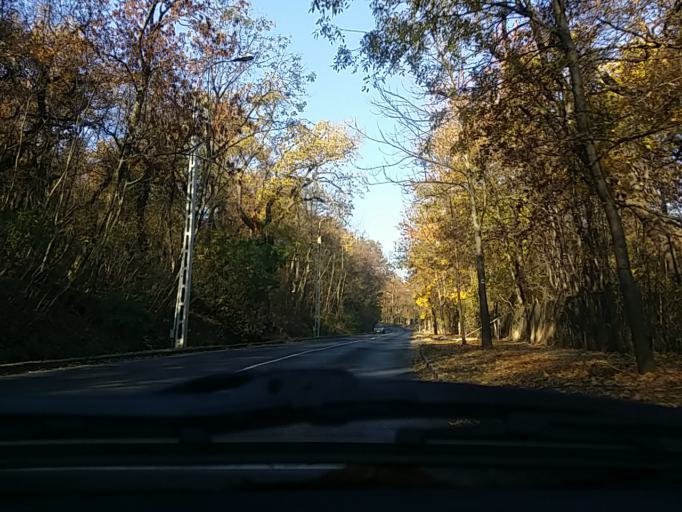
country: HU
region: Pest
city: Budakeszi
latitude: 47.5220
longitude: 18.9667
